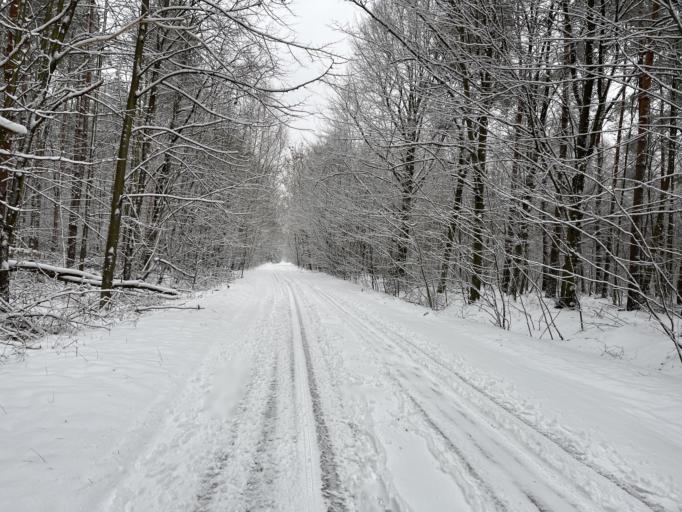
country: PL
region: Masovian Voivodeship
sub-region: Powiat zyrardowski
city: Guzow
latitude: 52.0469
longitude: 20.2725
